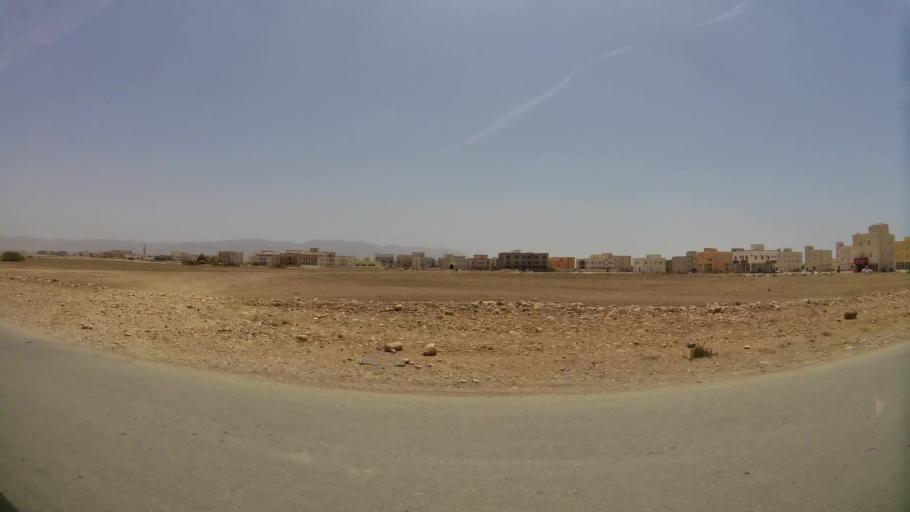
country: OM
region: Zufar
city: Salalah
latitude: 17.0509
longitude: 54.2090
